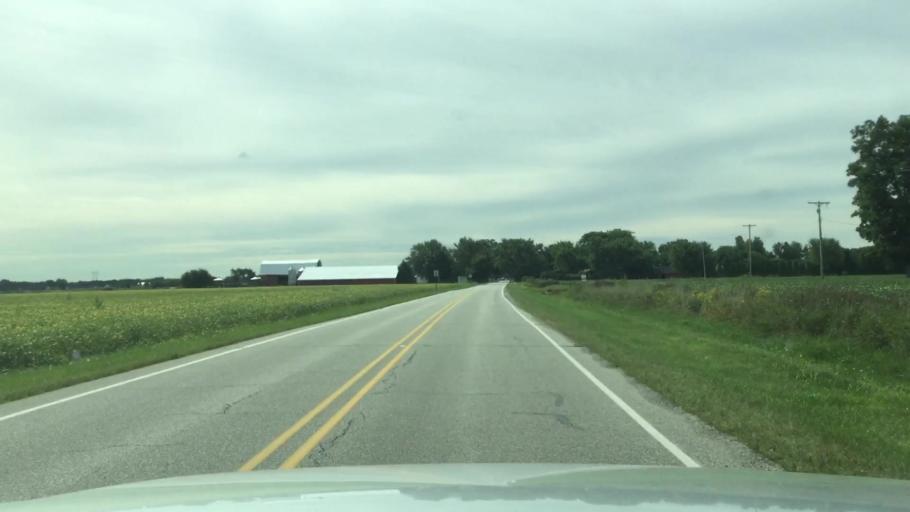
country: US
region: Michigan
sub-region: Genesee County
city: Montrose
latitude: 43.1318
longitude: -83.9881
